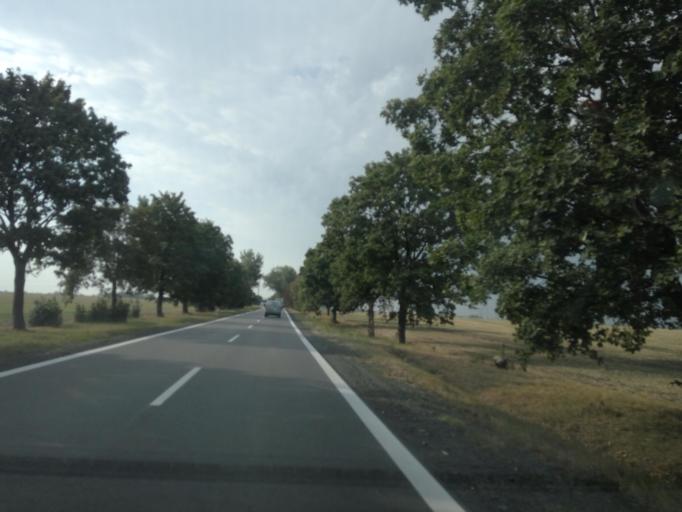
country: PL
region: Lower Silesian Voivodeship
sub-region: Powiat wroclawski
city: Zerniki Wroclawskie
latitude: 51.0147
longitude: 17.0644
